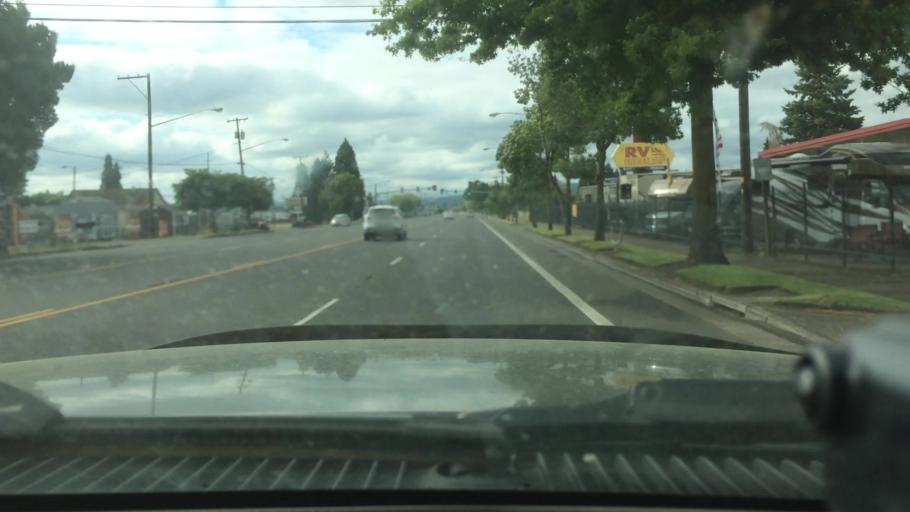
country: US
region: Oregon
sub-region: Lane County
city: Eugene
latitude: 44.0821
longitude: -123.1529
